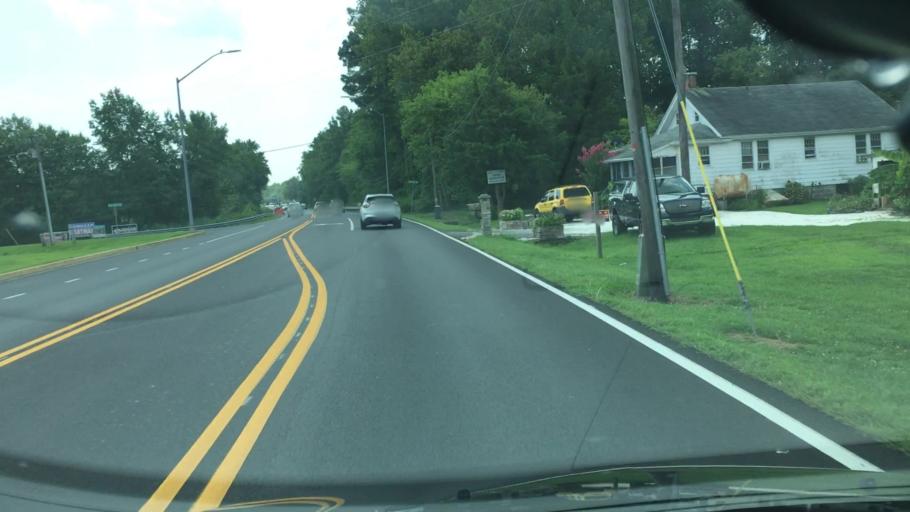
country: US
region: Maryland
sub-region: Worcester County
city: Ocean Pines
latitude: 38.3593
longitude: -75.1690
